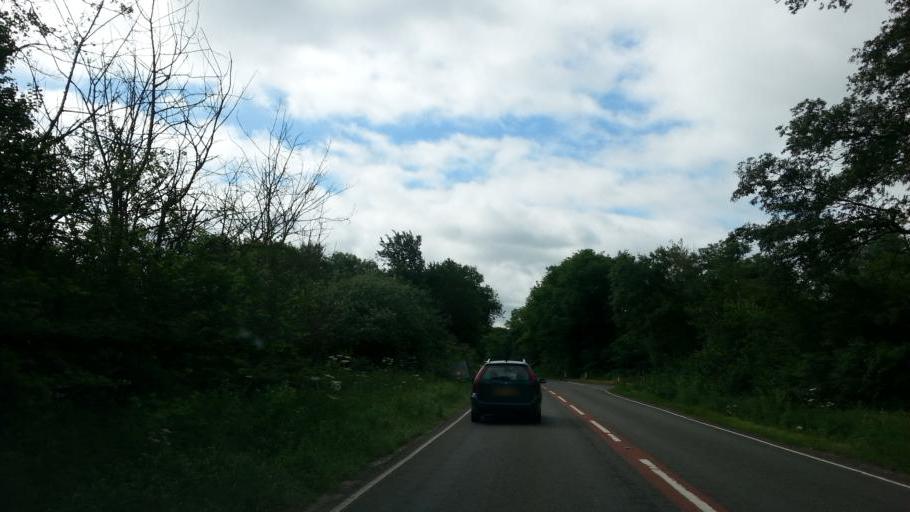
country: GB
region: England
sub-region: Cambridgeshire
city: Papworth Everard
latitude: 52.2773
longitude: -0.1385
